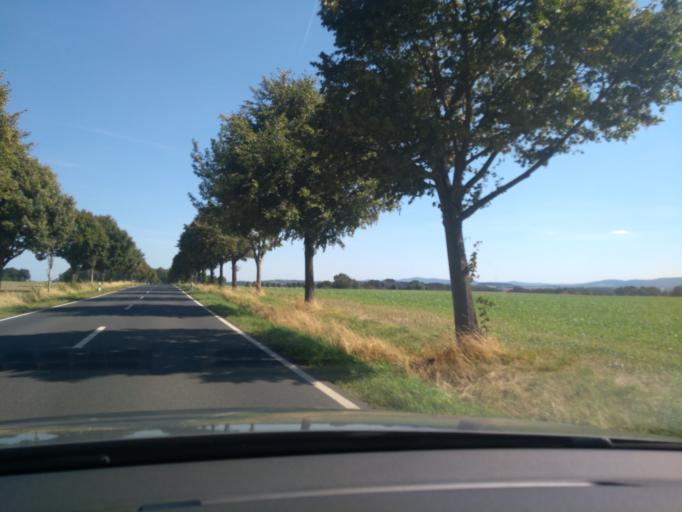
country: DE
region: Saxony
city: Crostwitz
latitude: 51.2137
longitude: 14.2766
